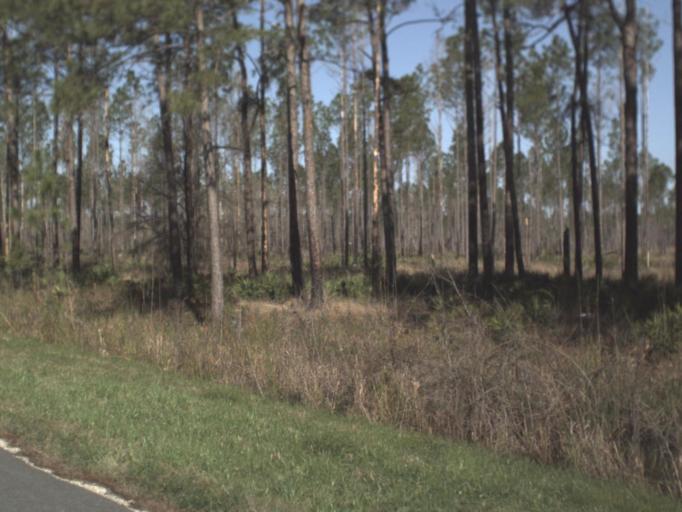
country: US
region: Florida
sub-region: Leon County
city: Woodville
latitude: 30.1905
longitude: -84.0604
